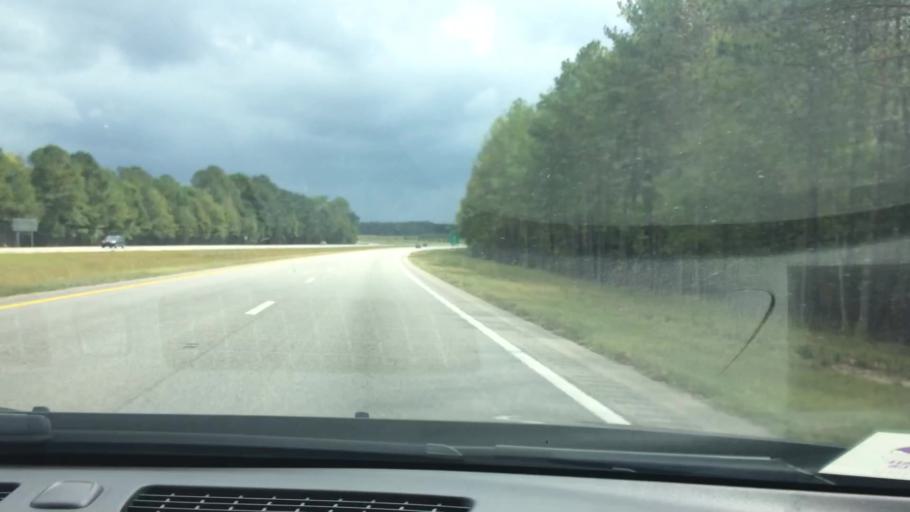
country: US
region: North Carolina
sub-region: Wilson County
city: Lucama
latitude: 35.7677
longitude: -78.0355
